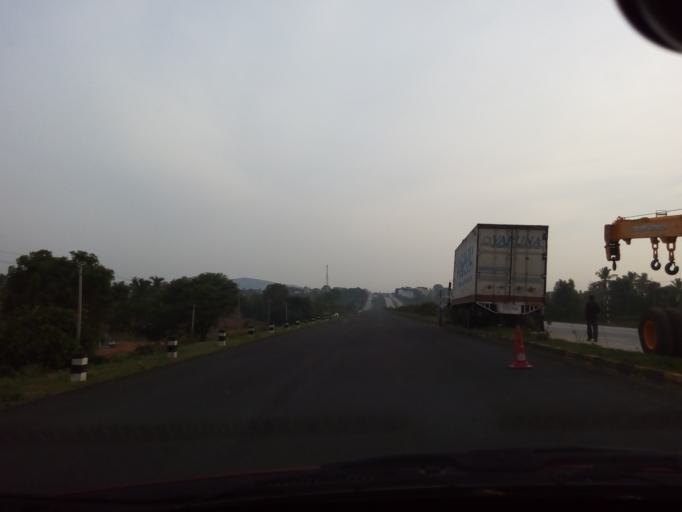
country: IN
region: Karnataka
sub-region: Chikkaballapur
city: Gudibanda
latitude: 13.5778
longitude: 77.7816
